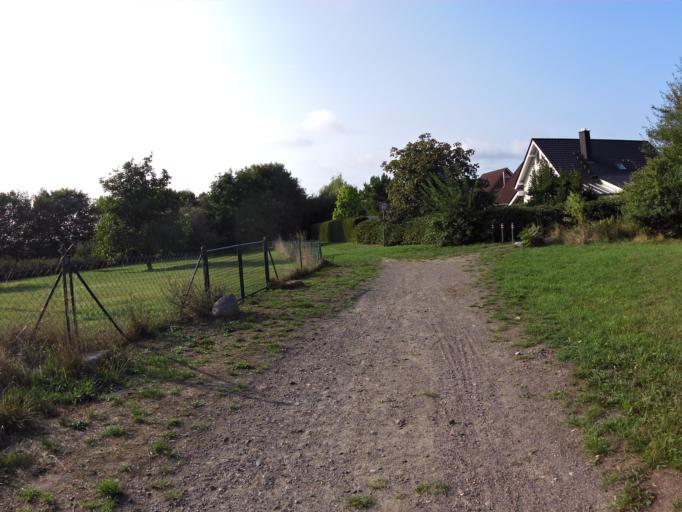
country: DE
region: Mecklenburg-Vorpommern
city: Seebad Bansin
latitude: 53.9549
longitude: 14.1468
